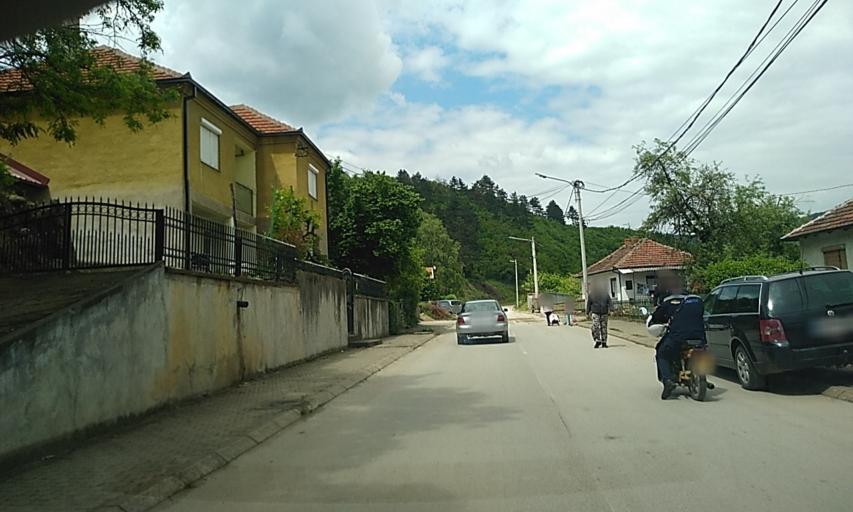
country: RS
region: Central Serbia
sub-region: Pcinjski Okrug
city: Vladicin Han
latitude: 42.7161
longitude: 22.0638
